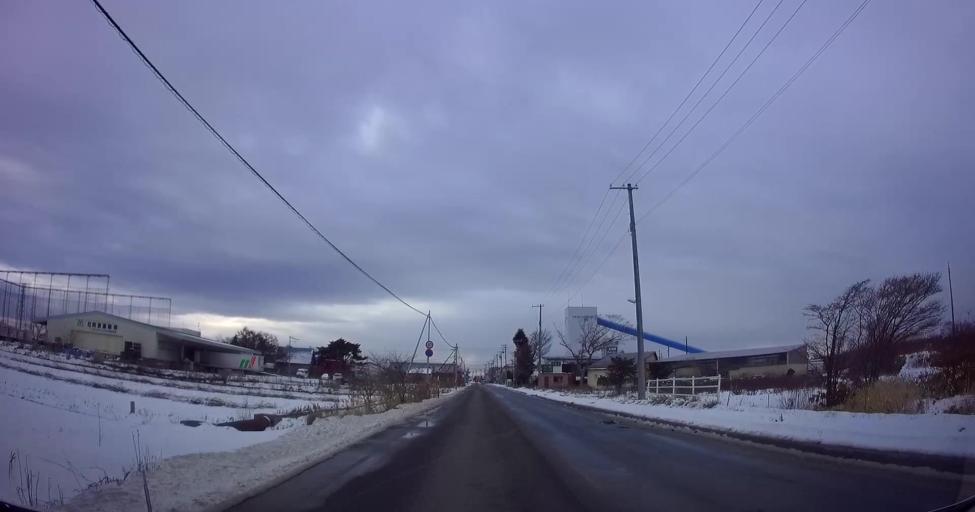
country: JP
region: Hokkaido
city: Kamiiso
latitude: 41.8303
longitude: 140.6877
